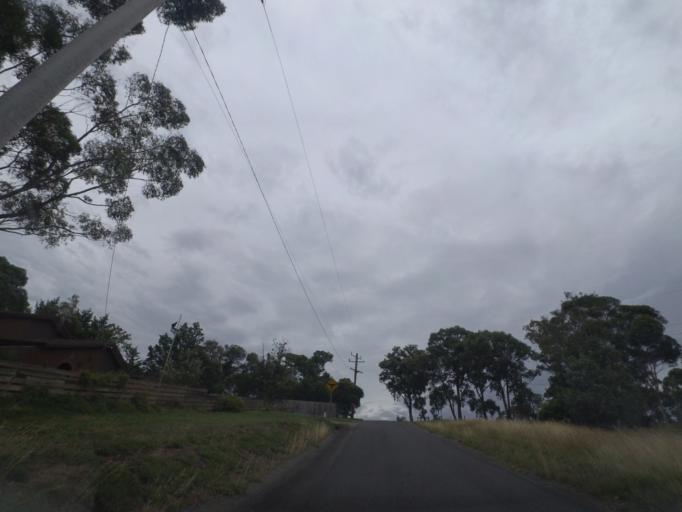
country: AU
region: Victoria
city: Plenty
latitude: -37.6592
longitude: 145.1294
